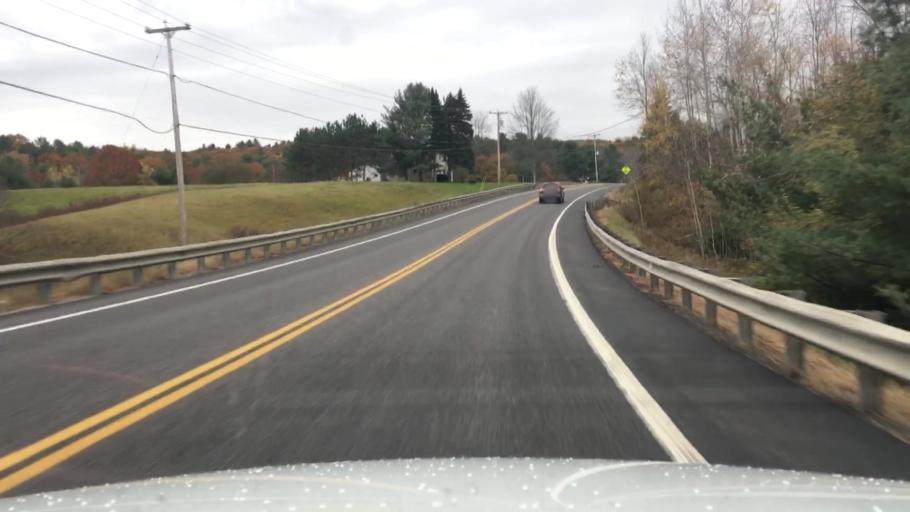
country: US
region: Maine
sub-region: Kennebec County
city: Pittston
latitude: 44.1898
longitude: -69.7465
